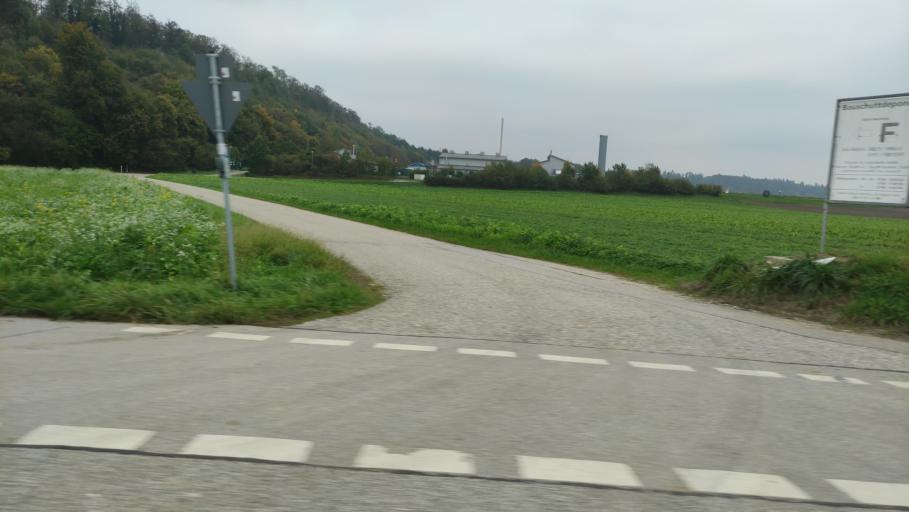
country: DE
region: Bavaria
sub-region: Upper Bavaria
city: Burghausen
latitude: 48.1922
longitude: 12.8545
